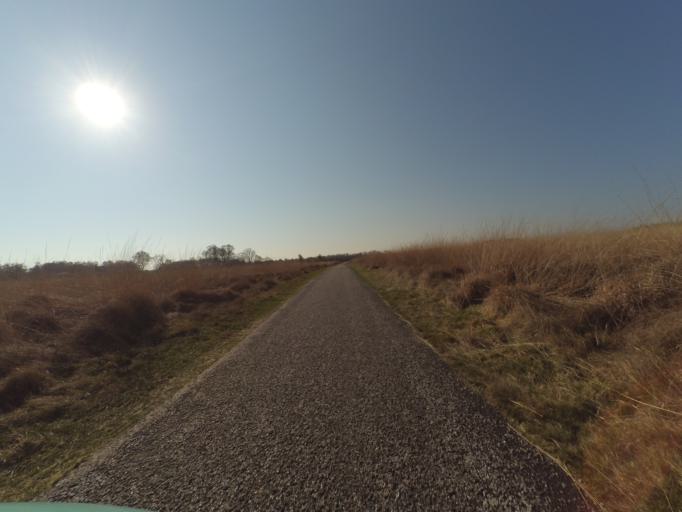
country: NL
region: Gelderland
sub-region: Gemeente Arnhem
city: Hoogkamp
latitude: 52.0650
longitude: 5.8476
